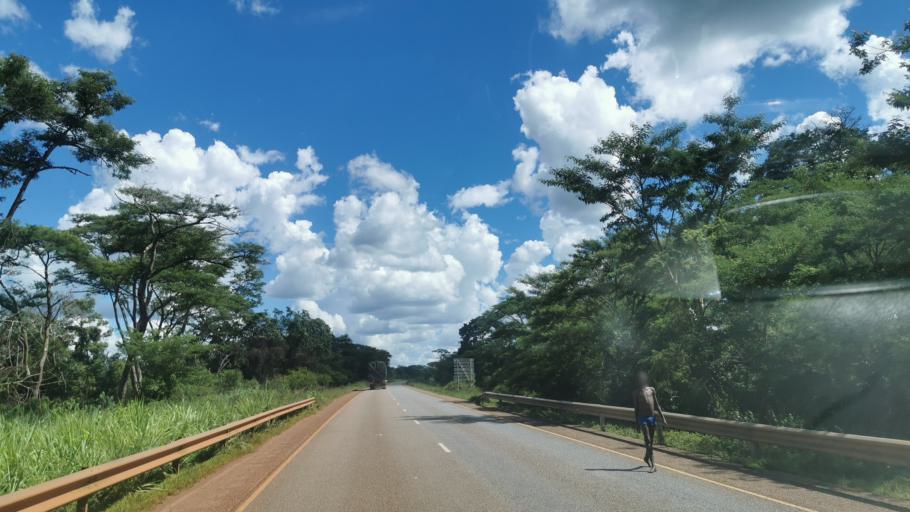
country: TZ
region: Geita
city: Uyovu
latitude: -3.0507
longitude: 31.2545
